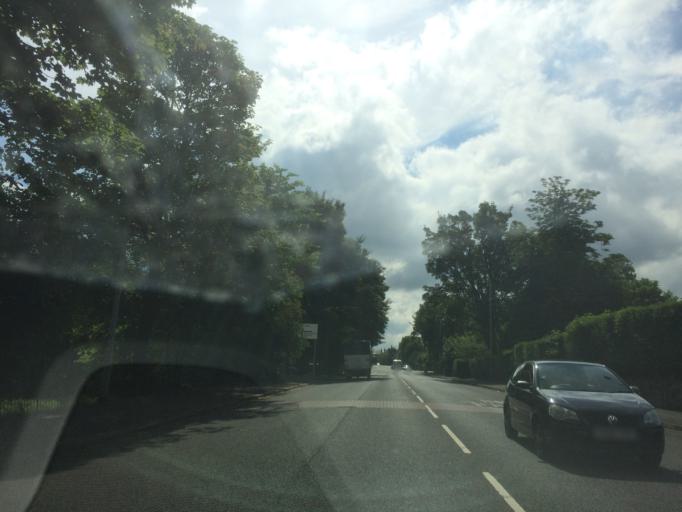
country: GB
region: Scotland
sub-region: East Renfrewshire
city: Giffnock
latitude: 55.8171
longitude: -4.2907
